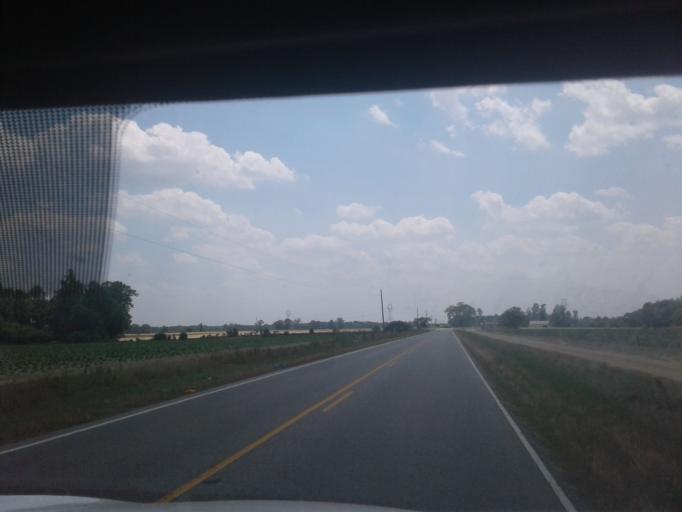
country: US
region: North Carolina
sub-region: Harnett County
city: Erwin
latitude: 35.3583
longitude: -78.6372
